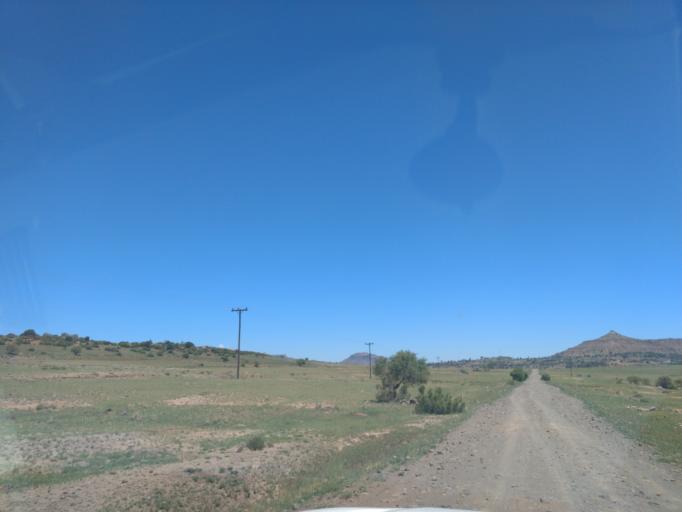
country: LS
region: Maseru
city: Maseru
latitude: -29.4704
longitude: 27.3755
